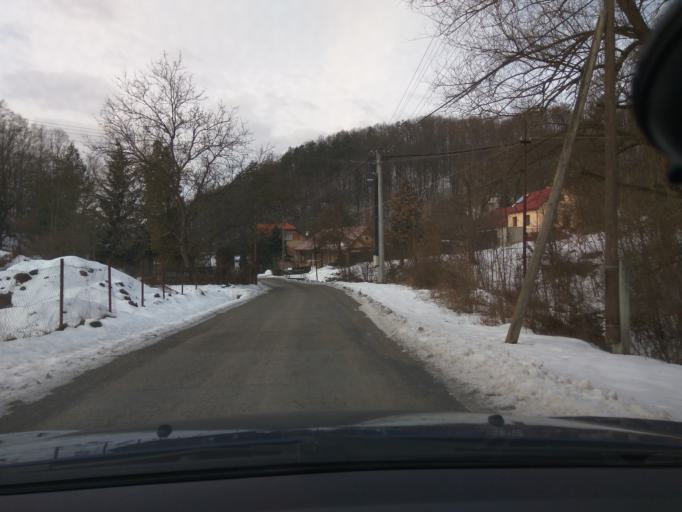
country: SK
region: Banskobystricky
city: Zarnovica
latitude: 48.4846
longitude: 18.7383
